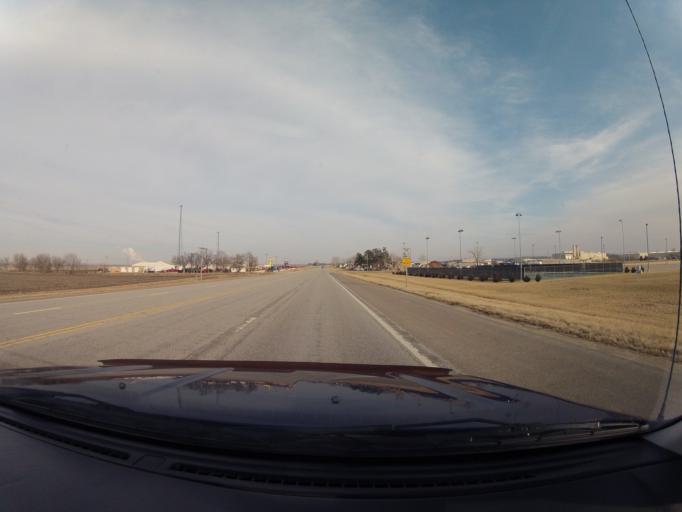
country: US
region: Kansas
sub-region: Pottawatomie County
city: Wamego
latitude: 39.2100
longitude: -96.2987
